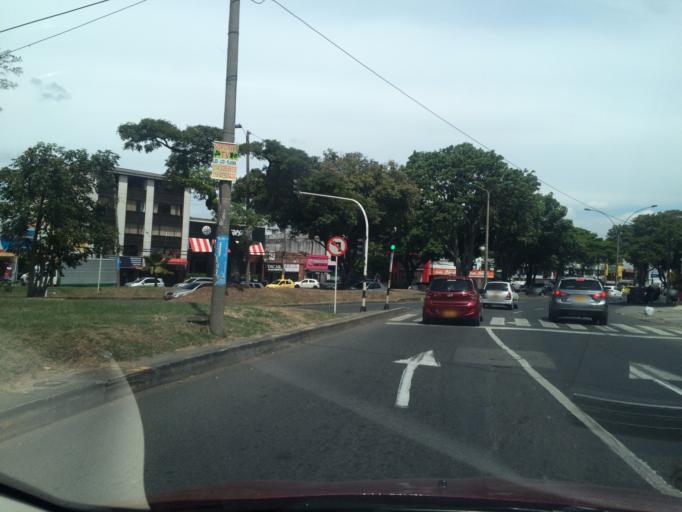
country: CO
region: Valle del Cauca
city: Cali
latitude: 3.4815
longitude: -76.5251
